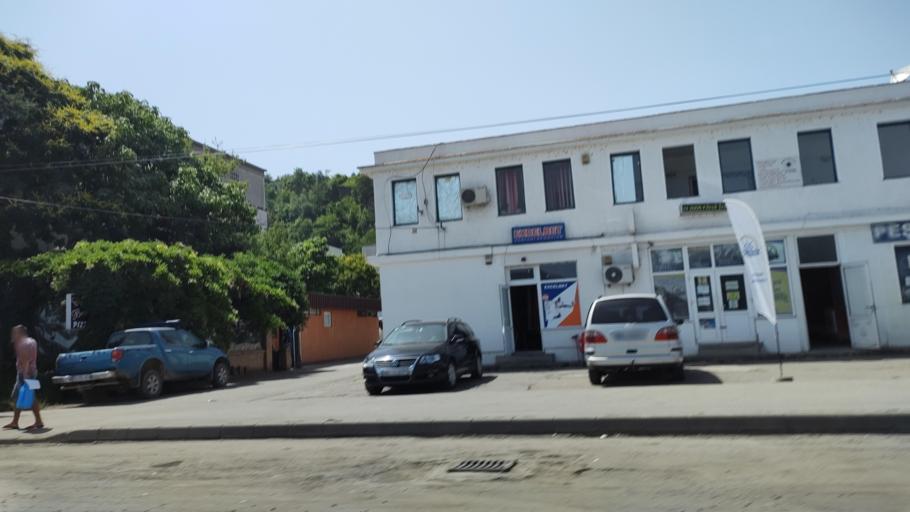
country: RO
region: Mehedinti
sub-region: Municipiul Orsova
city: Orsova
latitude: 44.7297
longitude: 22.4018
